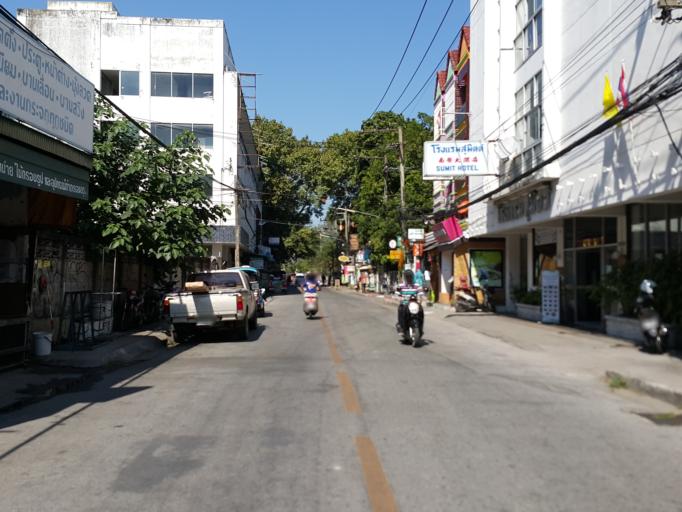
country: TH
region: Chiang Mai
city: Chiang Mai
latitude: 18.7919
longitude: 98.9901
